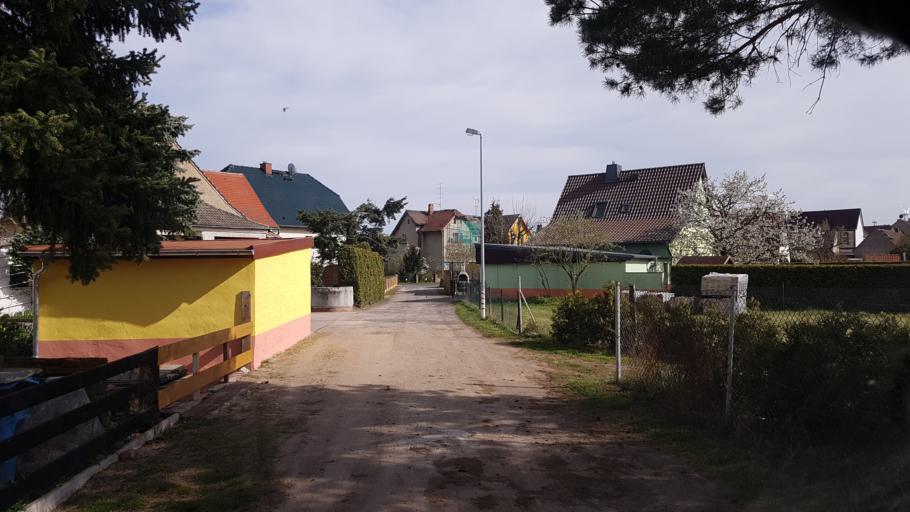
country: DE
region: Brandenburg
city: Falkenberg
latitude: 51.5887
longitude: 13.2974
